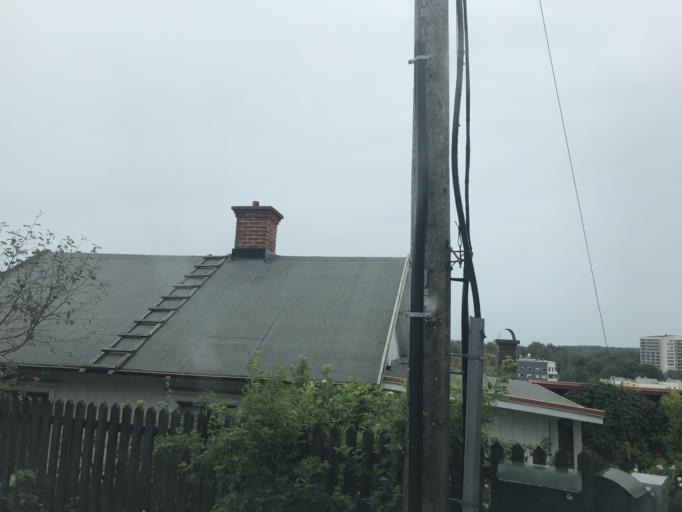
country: SE
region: Vaestra Goetaland
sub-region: Goteborg
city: Majorna
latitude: 57.7044
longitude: 11.9295
